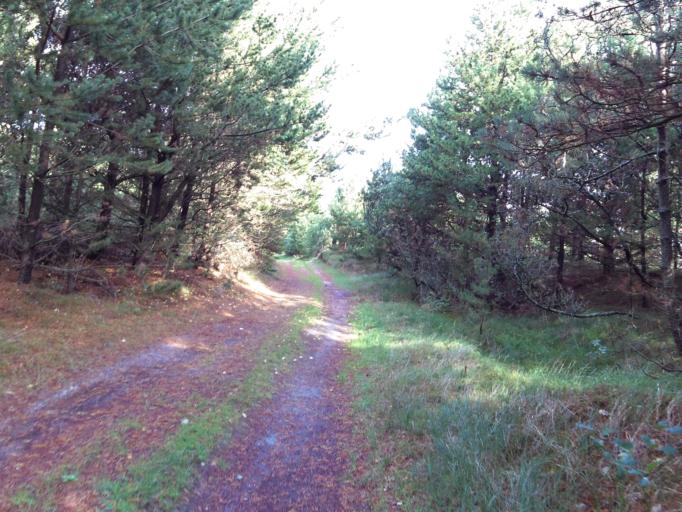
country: DK
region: South Denmark
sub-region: Varde Kommune
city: Oksbol
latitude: 55.5556
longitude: 8.2107
